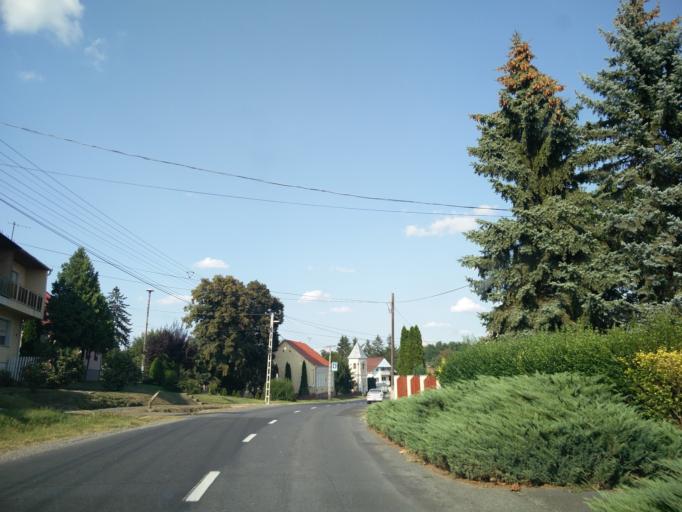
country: HU
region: Zala
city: Zalaegerszeg
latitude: 46.8727
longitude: 16.8674
